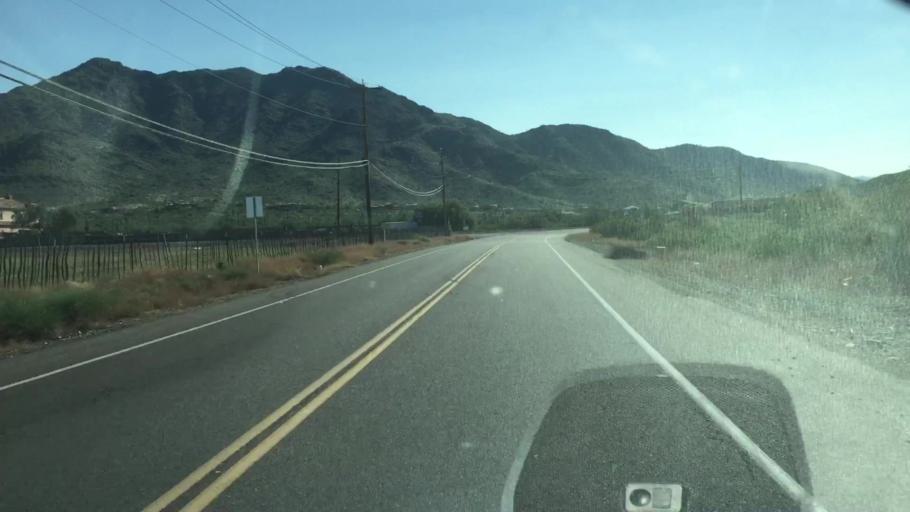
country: US
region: Arizona
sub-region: Maricopa County
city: Laveen
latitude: 33.3502
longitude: -112.1348
